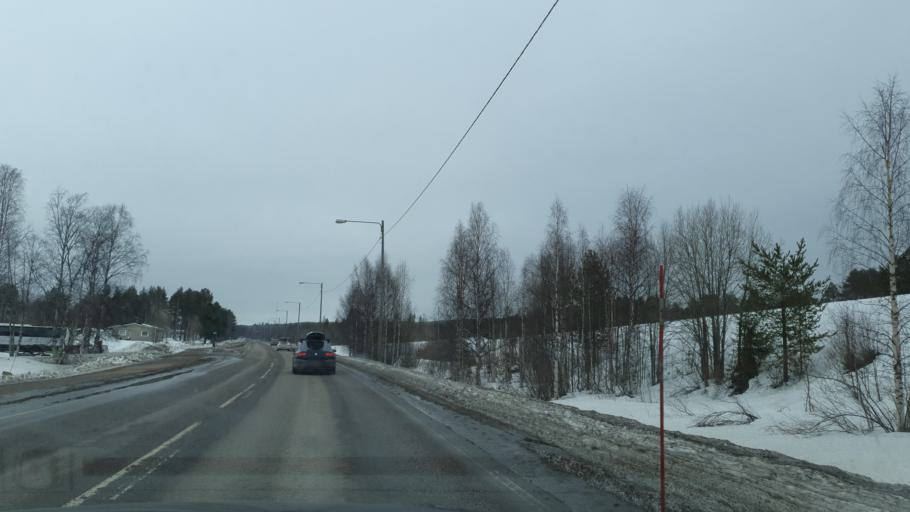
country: FI
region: Lapland
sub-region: Torniolaakso
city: Pello
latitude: 66.8146
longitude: 24.0004
